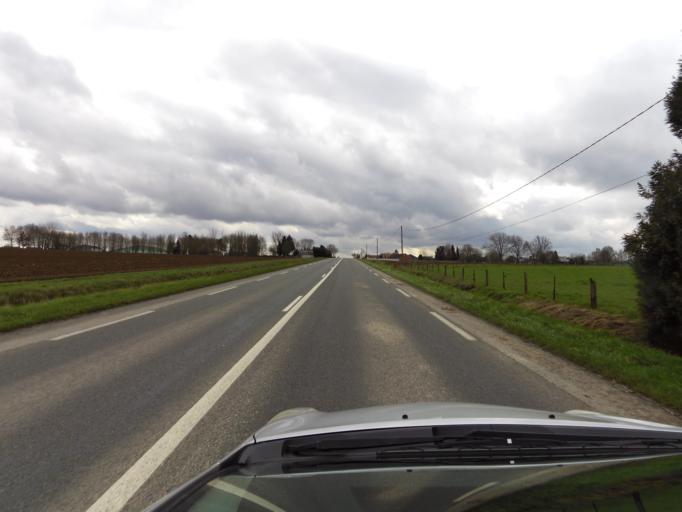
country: FR
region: Nord-Pas-de-Calais
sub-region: Departement du Pas-de-Calais
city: Beaurains
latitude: 50.2400
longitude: 2.7984
